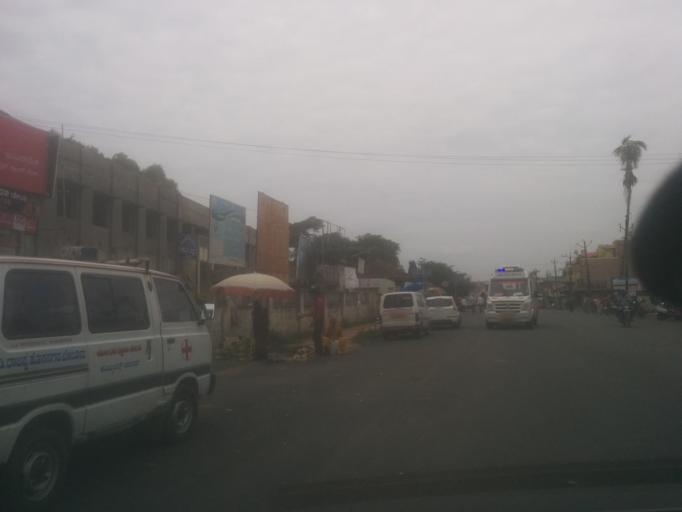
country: IN
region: Karnataka
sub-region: Hassan
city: Belur
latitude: 13.1641
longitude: 75.8648
